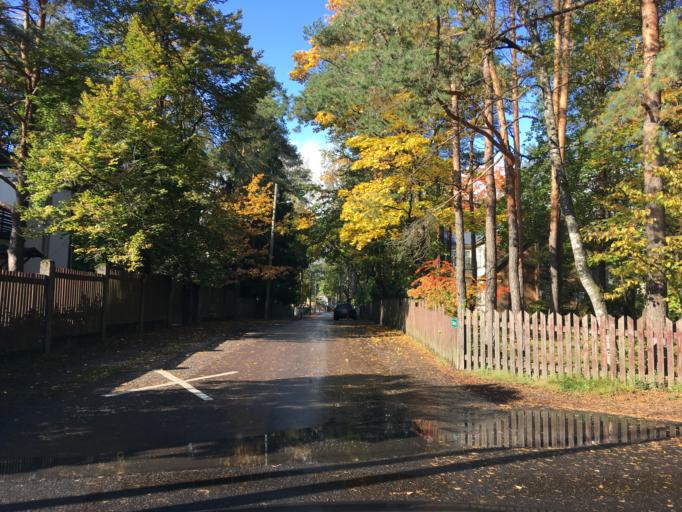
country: EE
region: Harju
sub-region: Tallinna linn
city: Tallinn
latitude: 59.3847
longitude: 24.7039
